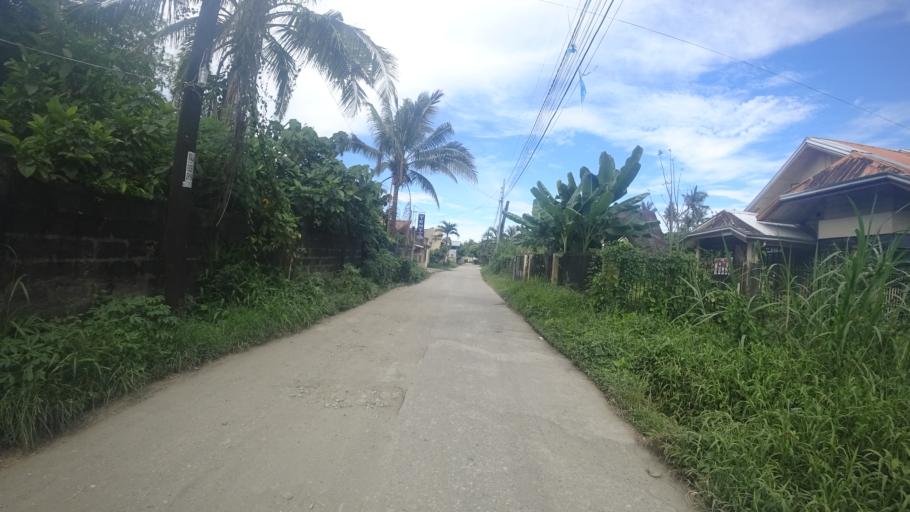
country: PH
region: Eastern Visayas
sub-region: Province of Leyte
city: Baras
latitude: 11.2043
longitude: 125.0088
